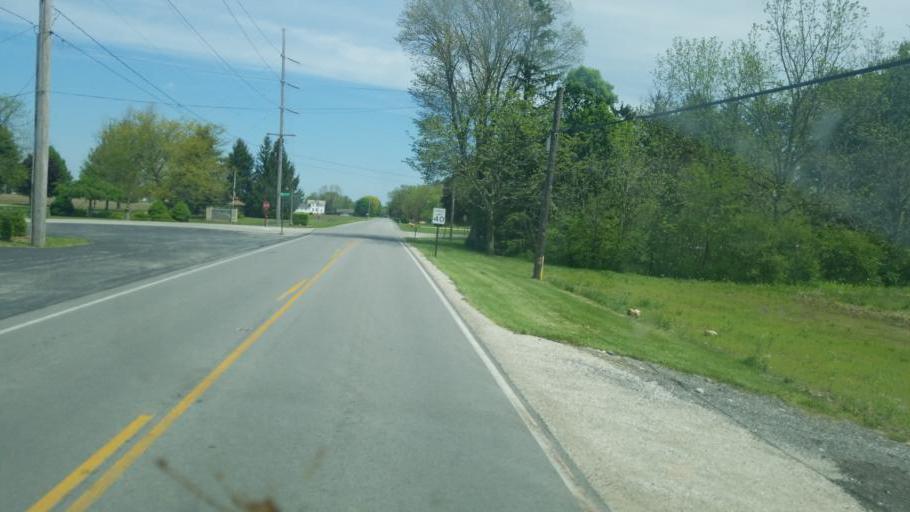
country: US
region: Ohio
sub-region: Sandusky County
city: Ballville
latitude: 41.3121
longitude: -83.1299
